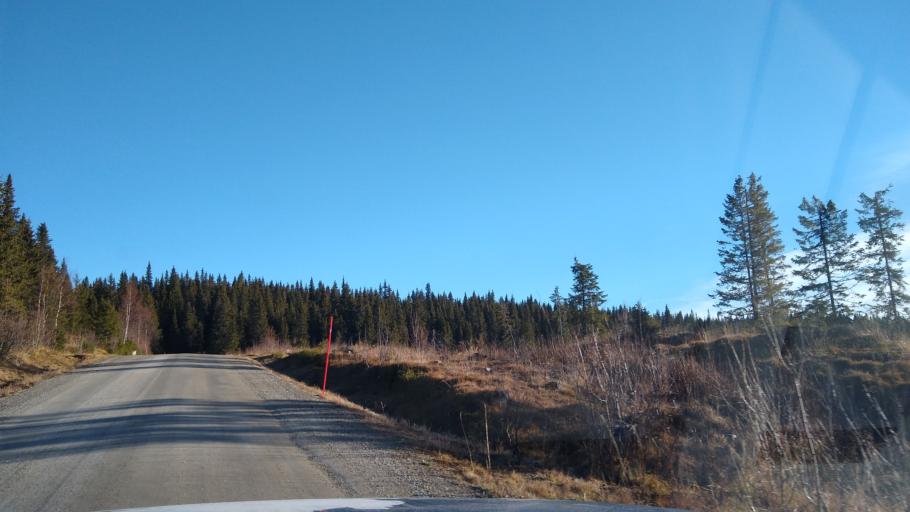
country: NO
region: Oppland
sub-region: Oyer
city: Tretten
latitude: 61.4025
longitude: 10.2812
